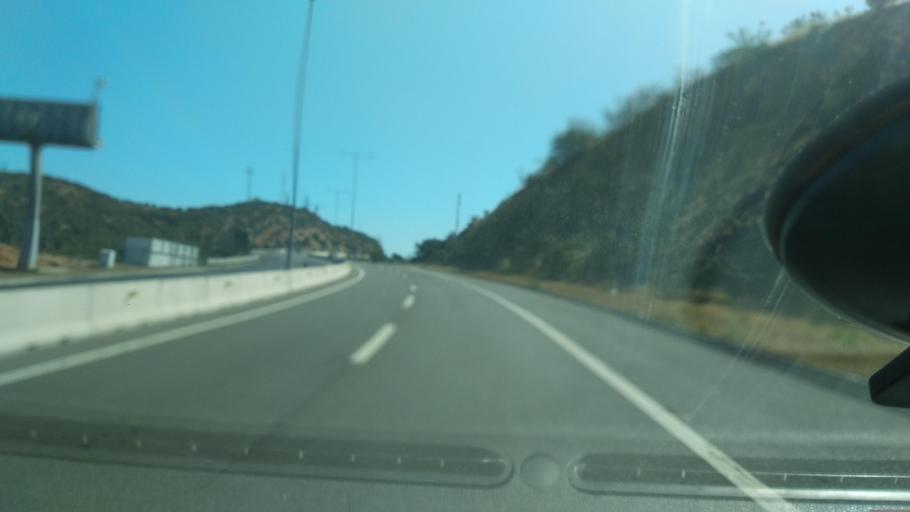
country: CL
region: Valparaiso
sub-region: Provincia de Marga Marga
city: Villa Alemana
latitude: -33.0450
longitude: -71.3238
